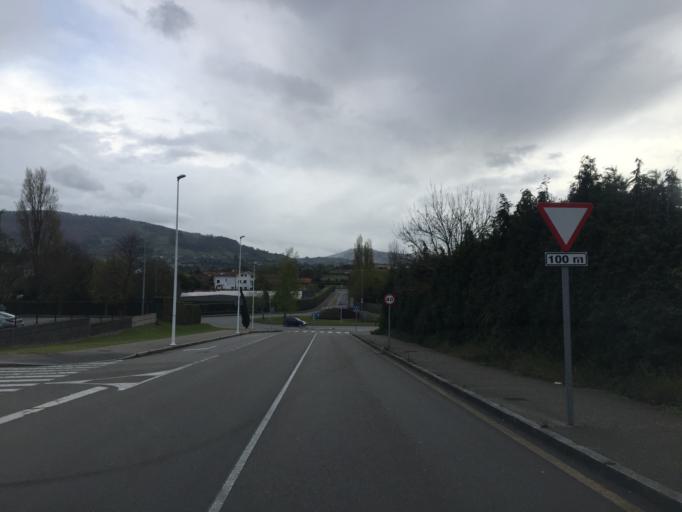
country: ES
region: Asturias
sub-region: Province of Asturias
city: Gijon
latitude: 43.5226
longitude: -5.6137
